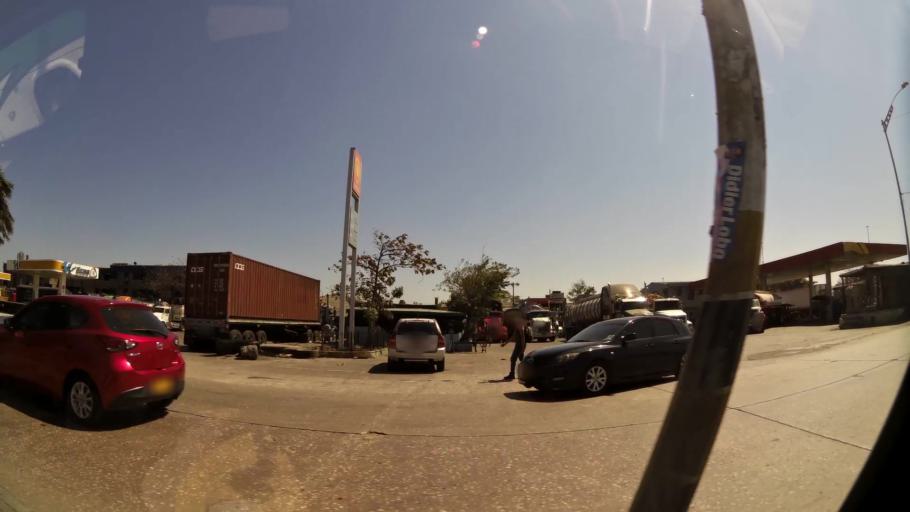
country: CO
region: Atlantico
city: Barranquilla
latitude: 10.9494
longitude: -74.7711
